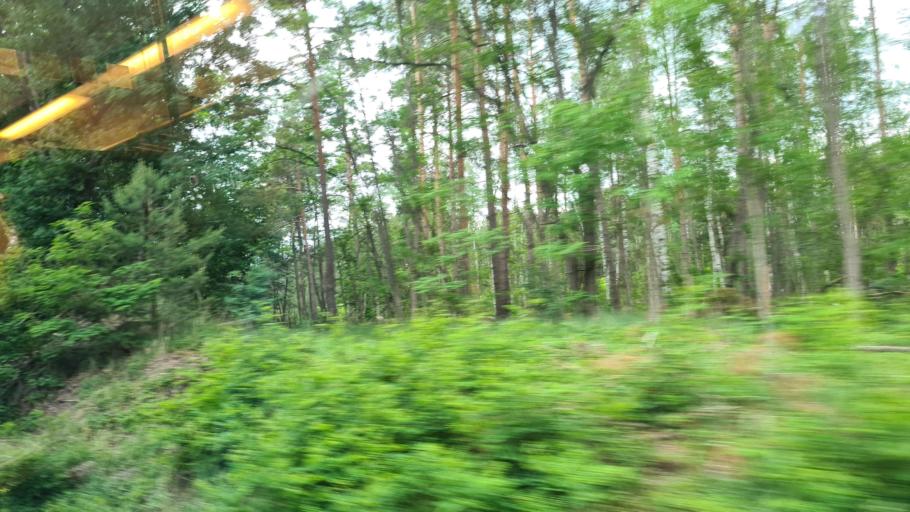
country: DE
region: Brandenburg
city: Schonborn
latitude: 51.6022
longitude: 13.4761
